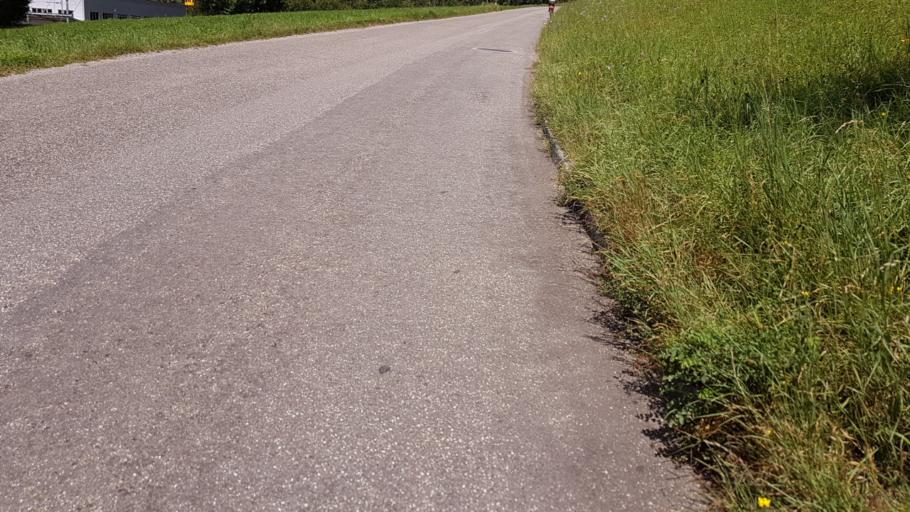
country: CH
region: Lucerne
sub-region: Entlebuch District
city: Oberdiessbach
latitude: 46.8468
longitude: 7.6219
